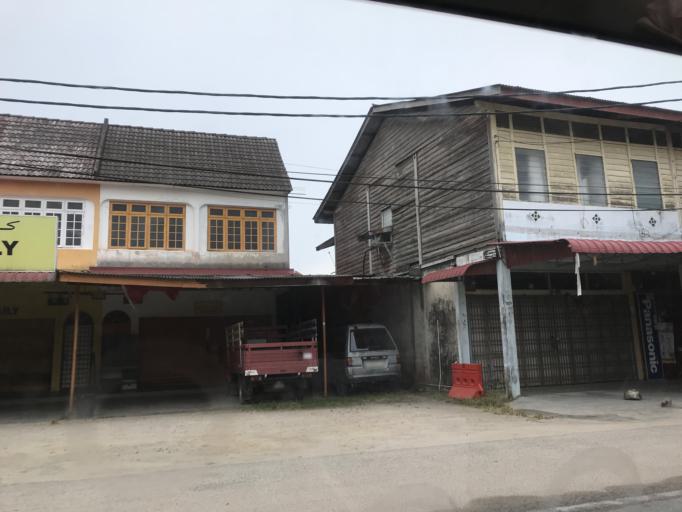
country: MY
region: Kelantan
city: Kota Bharu
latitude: 6.1212
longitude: 102.2016
